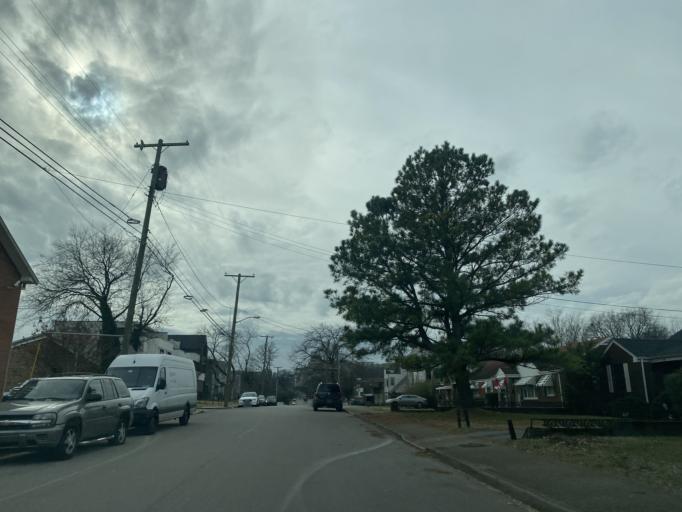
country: US
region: Tennessee
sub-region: Davidson County
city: Nashville
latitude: 36.1401
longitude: -86.7912
